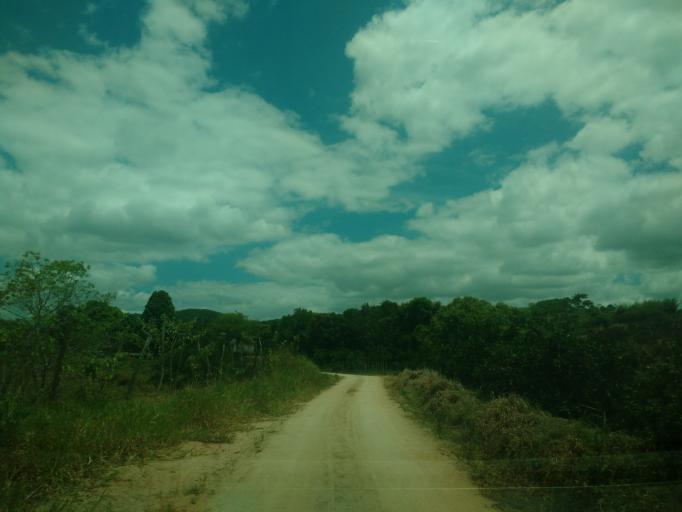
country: BR
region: Alagoas
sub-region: Santana Do Mundau
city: Santana do Mundau
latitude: -9.1569
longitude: -36.1658
